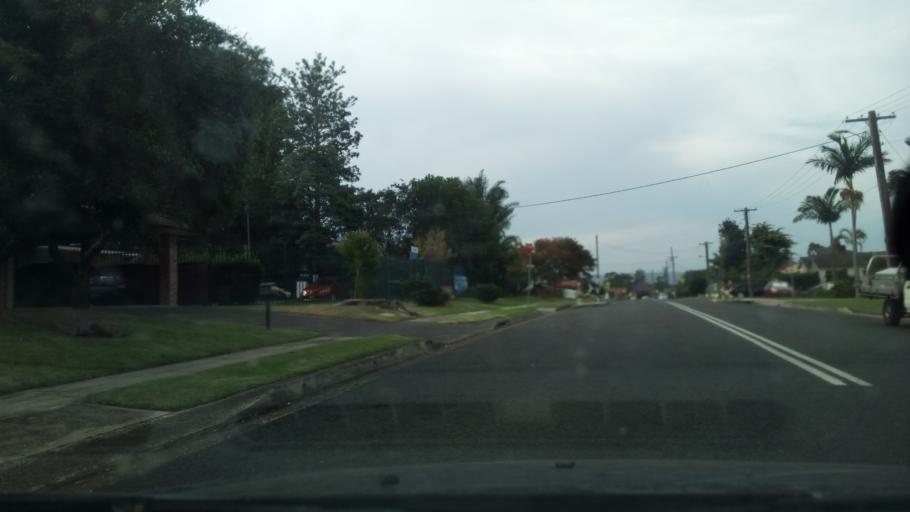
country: AU
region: New South Wales
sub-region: Wollongong
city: Fairy Meadow
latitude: -34.3995
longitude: 150.8895
